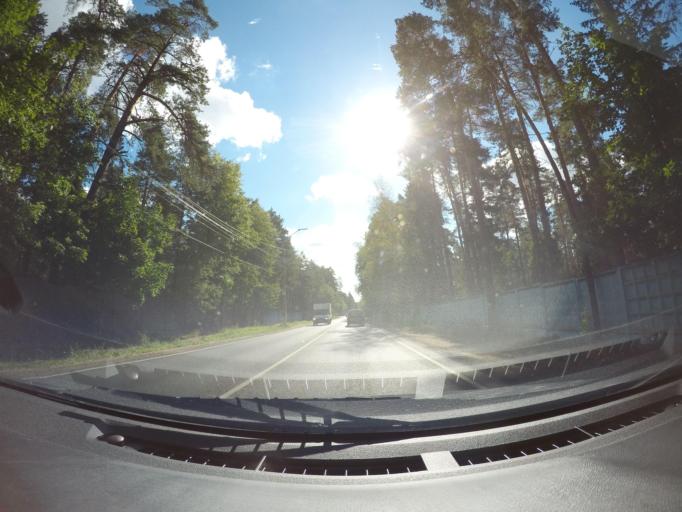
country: RU
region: Moskovskaya
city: Kratovo
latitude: 55.5994
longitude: 38.1761
